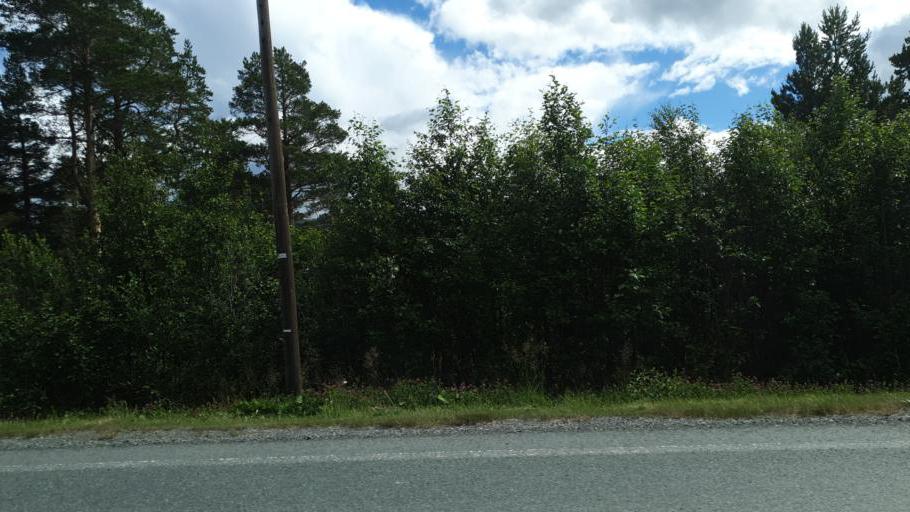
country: NO
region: Sor-Trondelag
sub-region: Rennebu
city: Berkak
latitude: 62.6773
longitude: 9.9193
